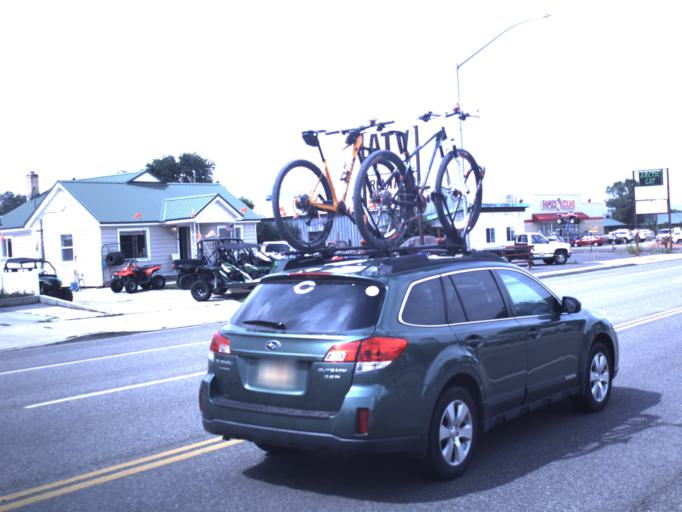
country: US
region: Utah
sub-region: Garfield County
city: Panguitch
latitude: 37.8297
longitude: -112.4357
